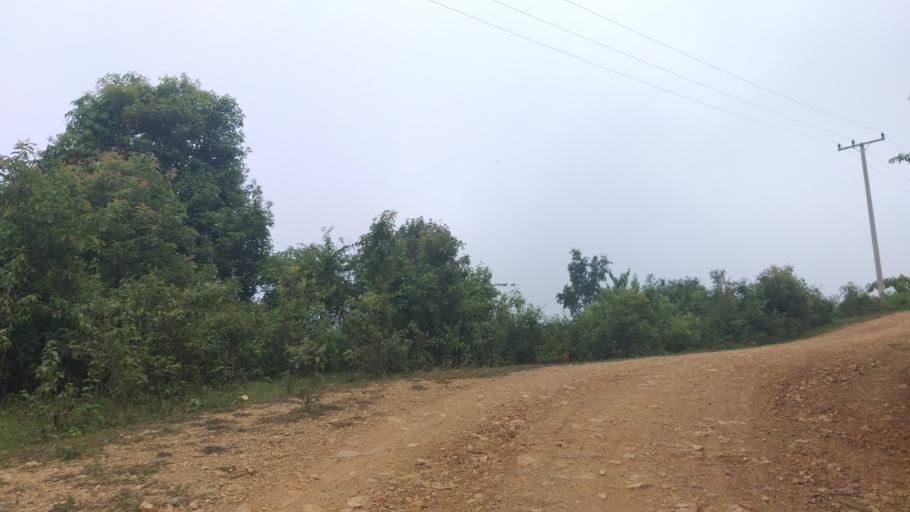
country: LA
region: Phongsali
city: Khoa
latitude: 21.2859
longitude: 102.6419
